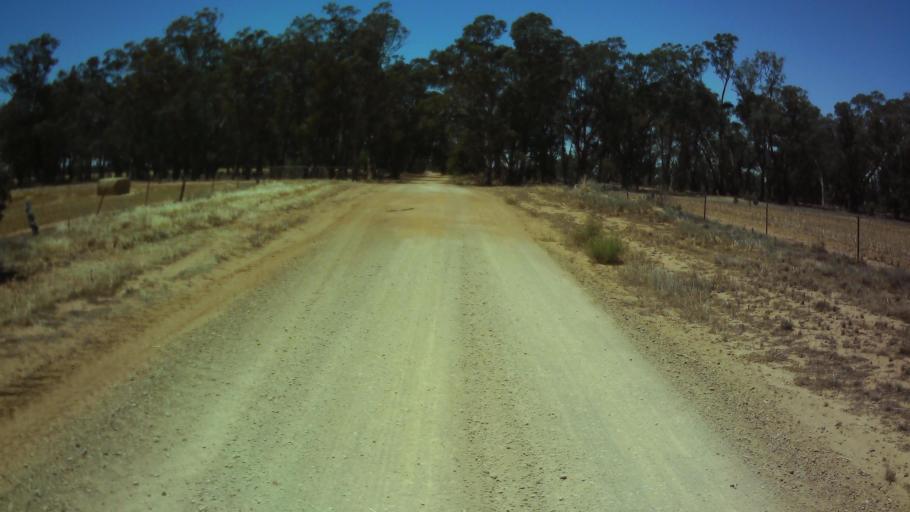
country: AU
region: New South Wales
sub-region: Weddin
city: Grenfell
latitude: -34.0436
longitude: 147.8021
